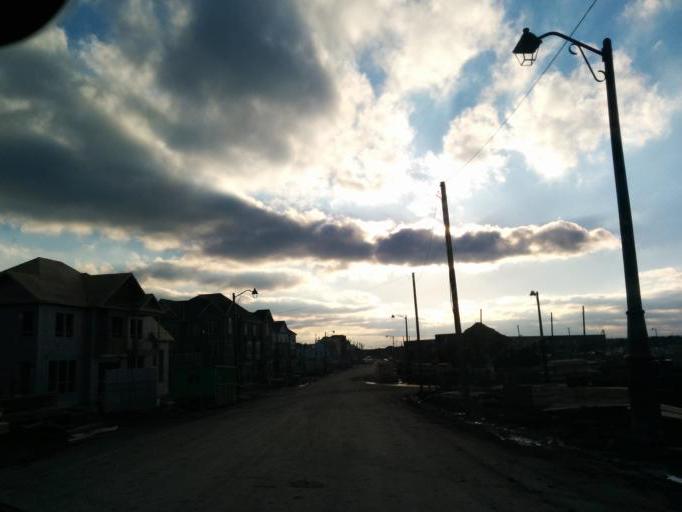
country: CA
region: Ontario
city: Oakville
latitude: 43.4736
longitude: -79.7411
